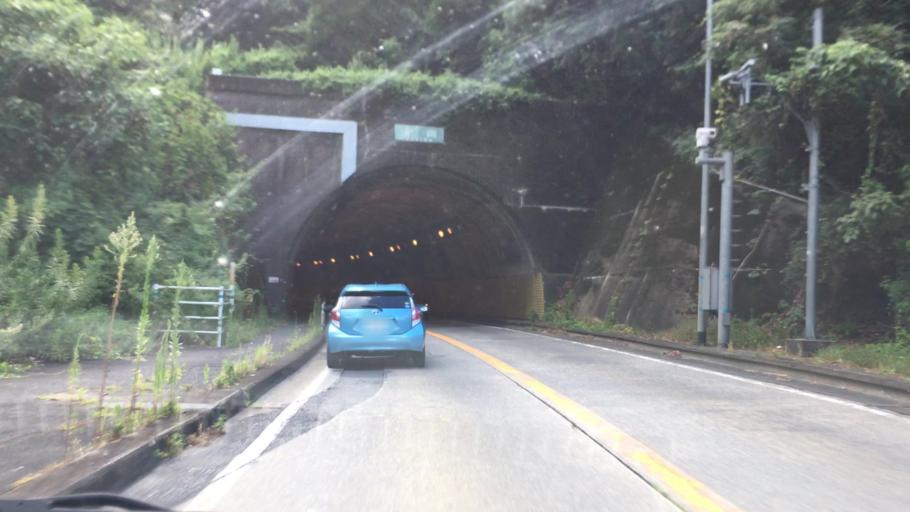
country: JP
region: Saga Prefecture
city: Imaricho-ko
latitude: 33.1886
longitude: 129.9027
